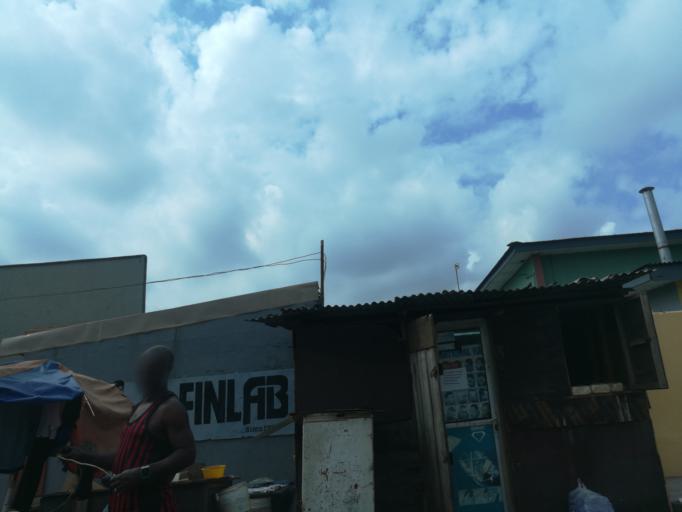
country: NG
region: Lagos
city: Somolu
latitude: 6.5602
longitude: 3.3624
